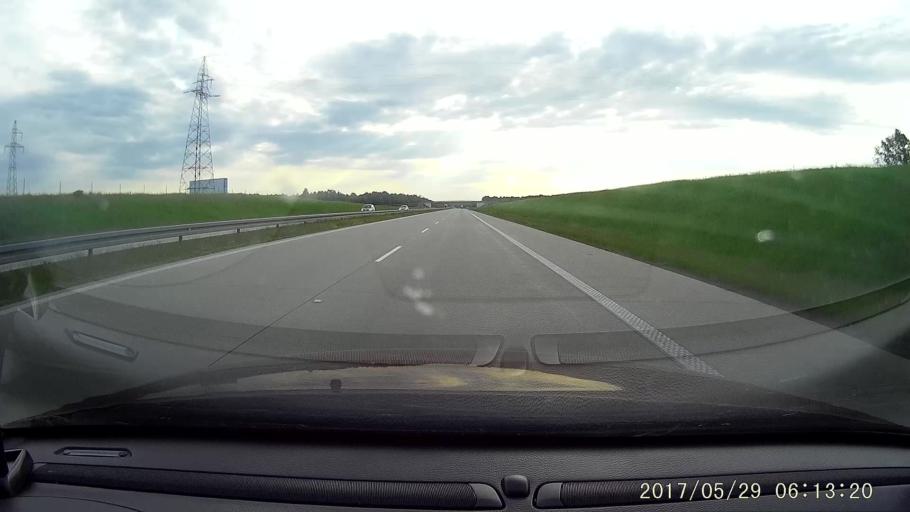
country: PL
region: Lower Silesian Voivodeship
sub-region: Powiat zgorzelecki
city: Wegliniec
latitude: 51.2265
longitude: 15.2999
